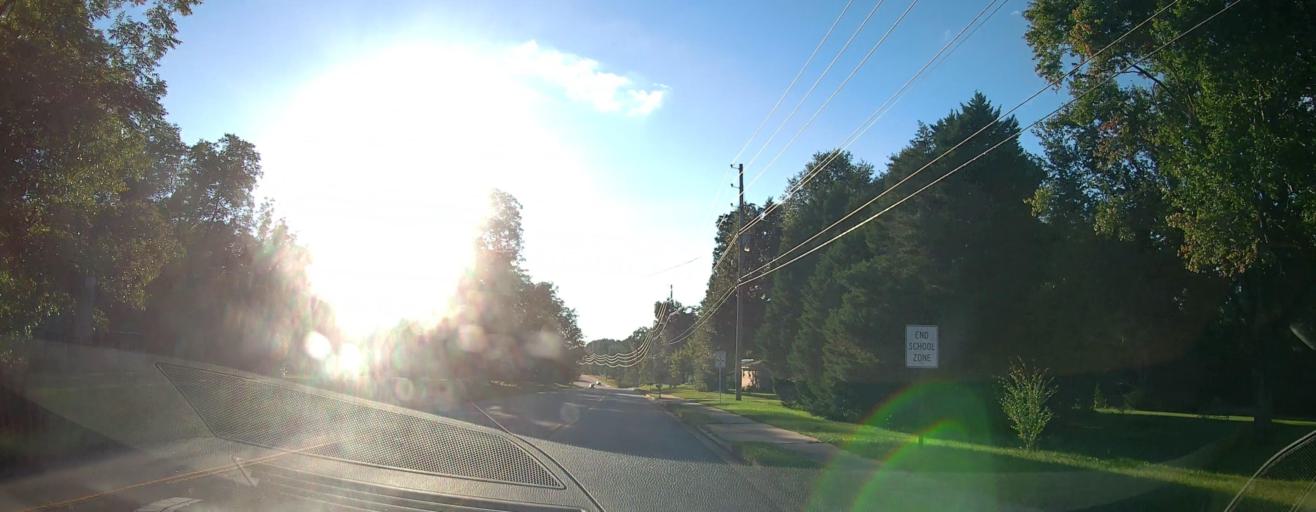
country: US
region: Georgia
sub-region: Houston County
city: Centerville
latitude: 32.6350
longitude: -83.6972
